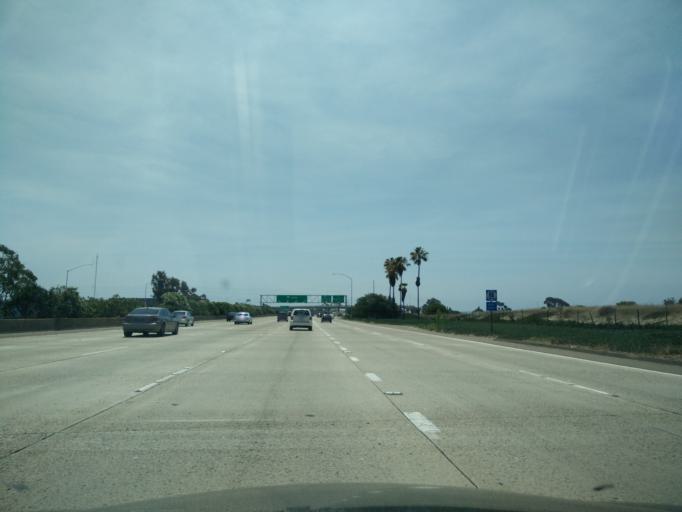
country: US
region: California
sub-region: San Diego County
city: San Diego
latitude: 32.7655
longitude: -117.2057
